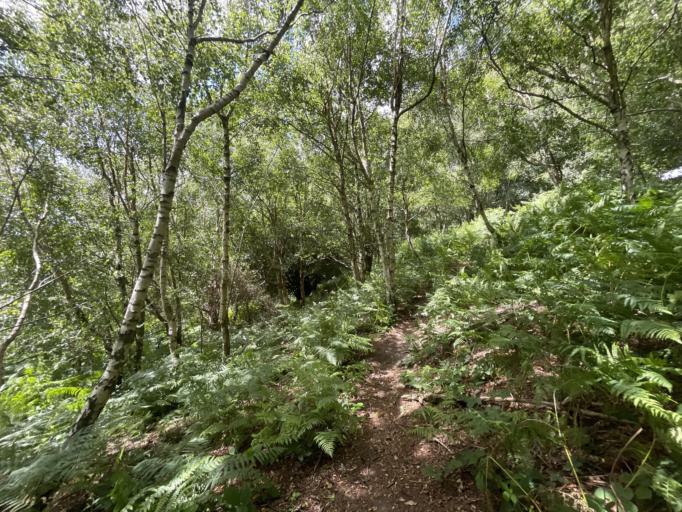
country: GB
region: England
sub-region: Kent
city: Edenbridge
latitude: 51.1642
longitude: 0.1344
